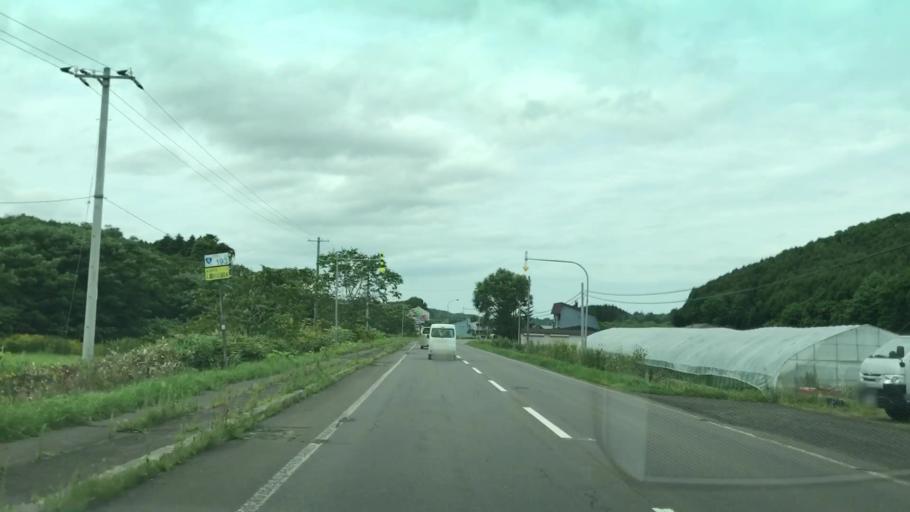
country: JP
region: Hokkaido
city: Iwanai
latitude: 42.9665
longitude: 140.6876
